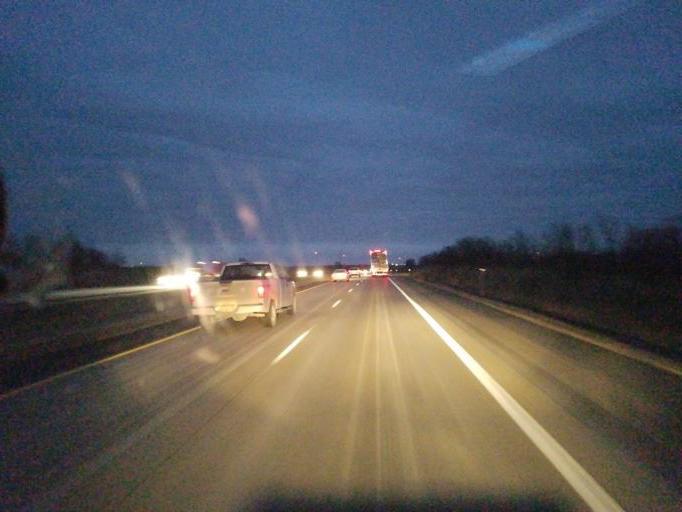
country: US
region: Iowa
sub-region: Cass County
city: Atlantic
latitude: 41.4965
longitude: -94.7358
